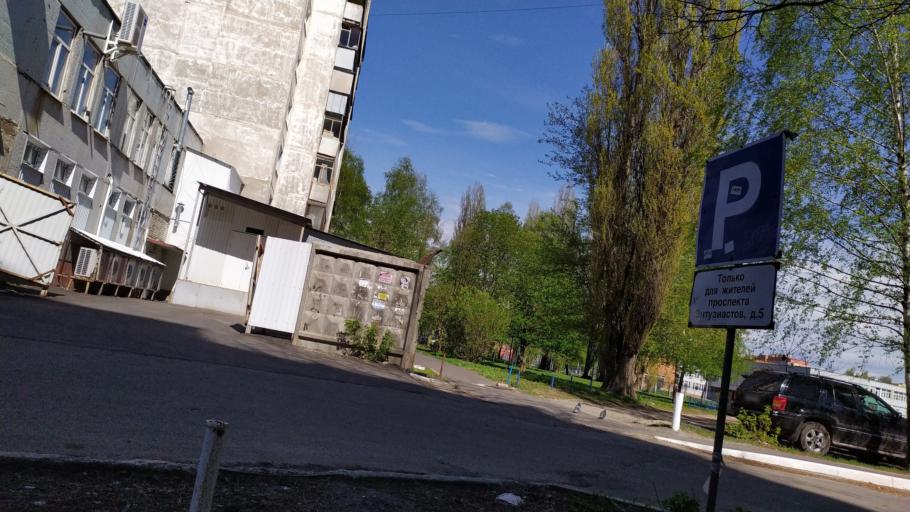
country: RU
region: Kursk
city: Kursk
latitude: 51.7413
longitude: 36.1366
